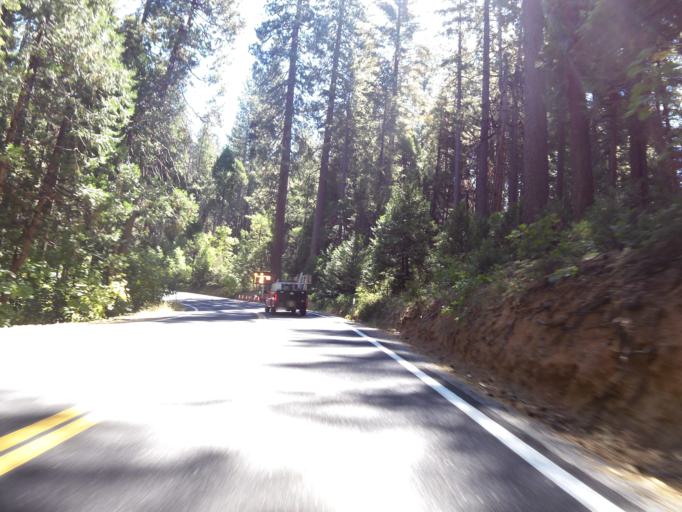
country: US
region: California
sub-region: Calaveras County
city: Arnold
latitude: 38.2687
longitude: -120.3268
